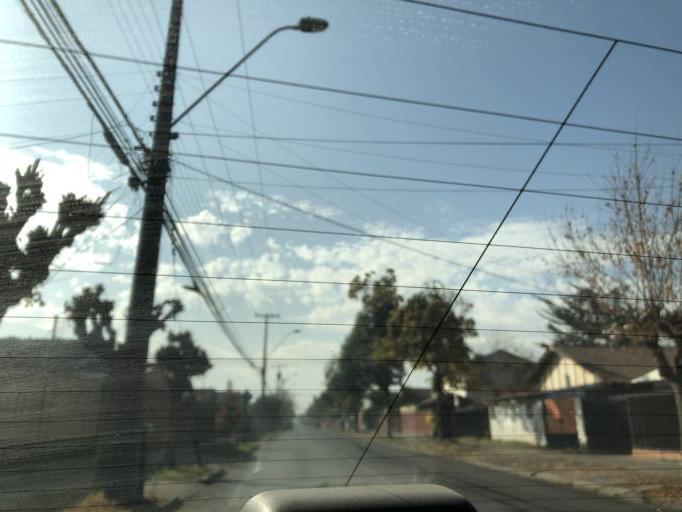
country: CL
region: Santiago Metropolitan
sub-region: Provincia de Cordillera
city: Puente Alto
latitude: -33.5920
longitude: -70.5772
